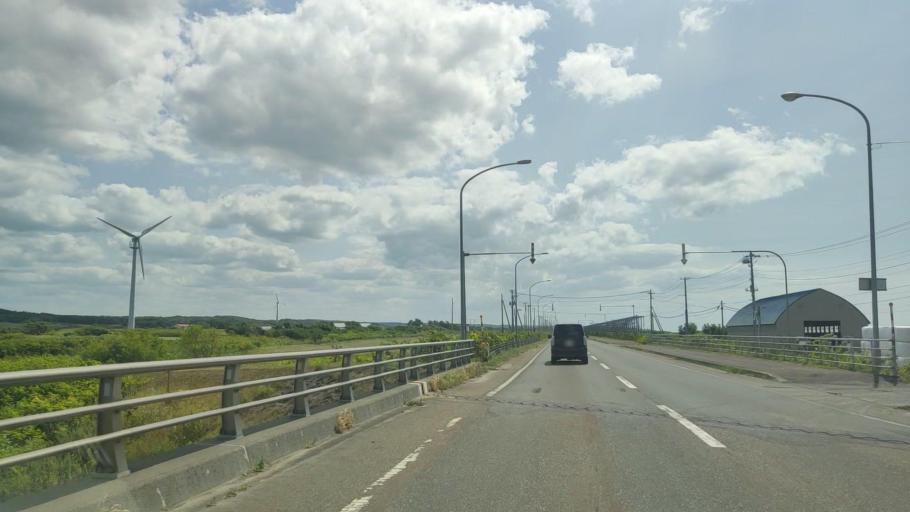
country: JP
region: Hokkaido
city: Makubetsu
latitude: 44.7531
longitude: 141.7951
